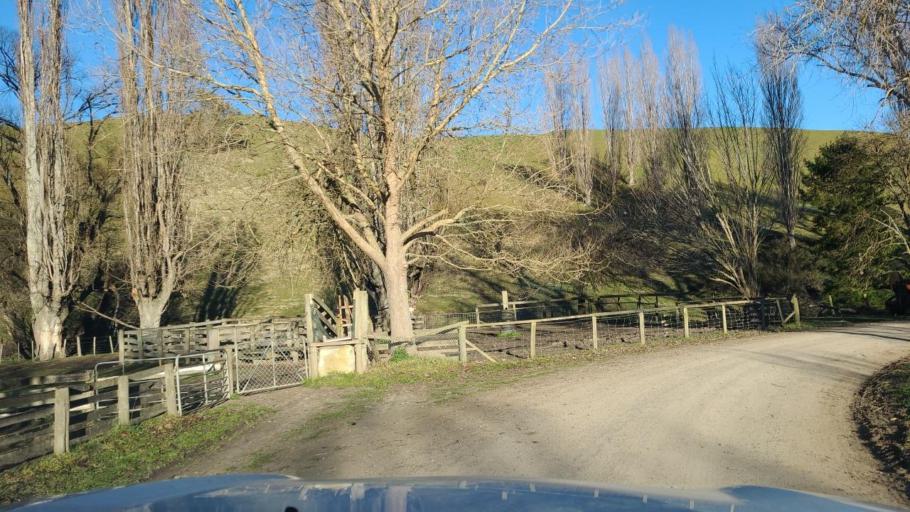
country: NZ
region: Hawke's Bay
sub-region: Hastings District
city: Hastings
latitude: -39.8014
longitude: 176.8361
